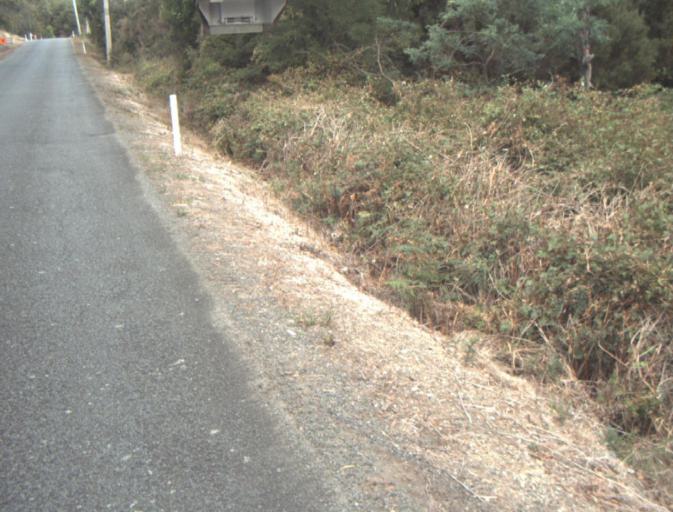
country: AU
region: Tasmania
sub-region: Launceston
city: Mayfield
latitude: -41.3001
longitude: 147.0329
